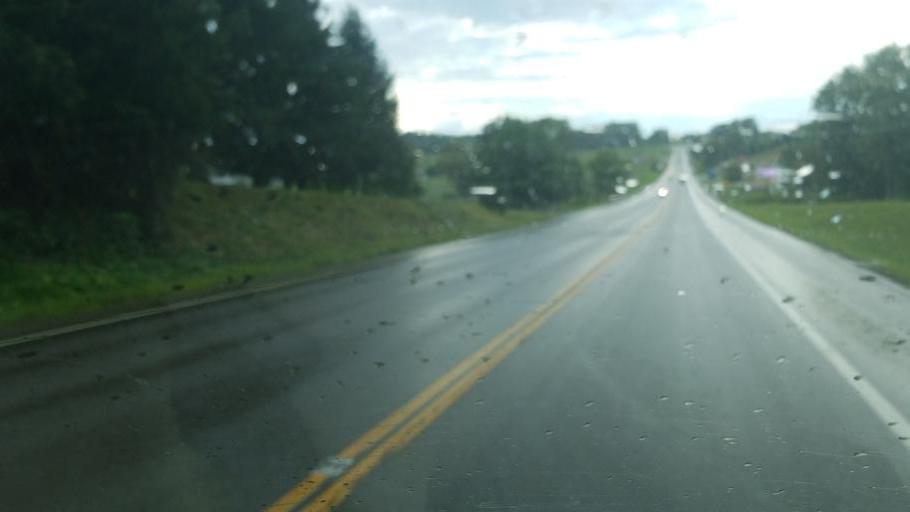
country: US
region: Ohio
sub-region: Holmes County
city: Millersburg
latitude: 40.5555
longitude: -81.8176
